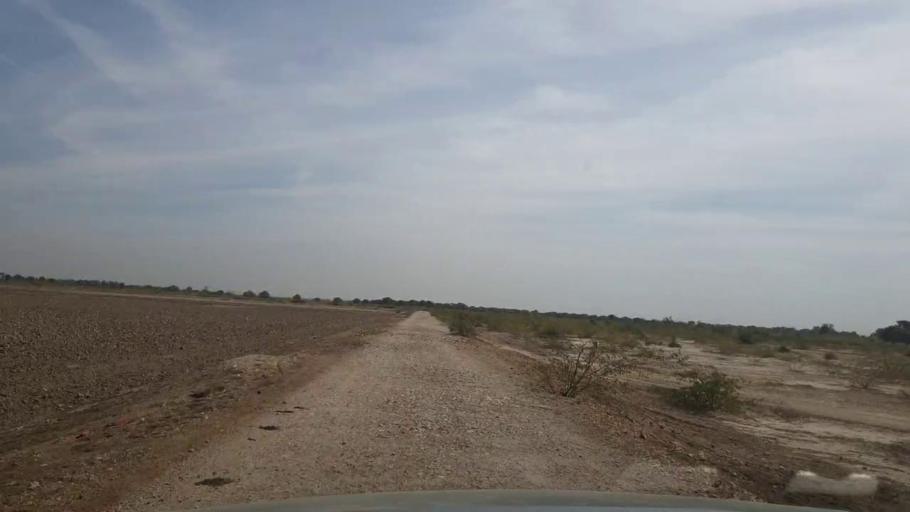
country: PK
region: Sindh
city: Nabisar
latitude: 25.1160
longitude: 69.6096
